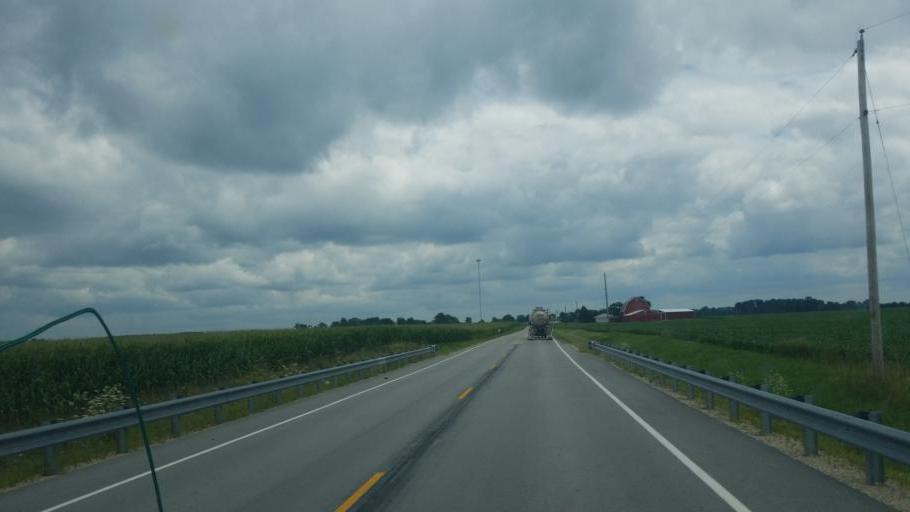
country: US
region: Indiana
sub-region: Wells County
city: Bluffton
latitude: 40.6549
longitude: -85.1637
